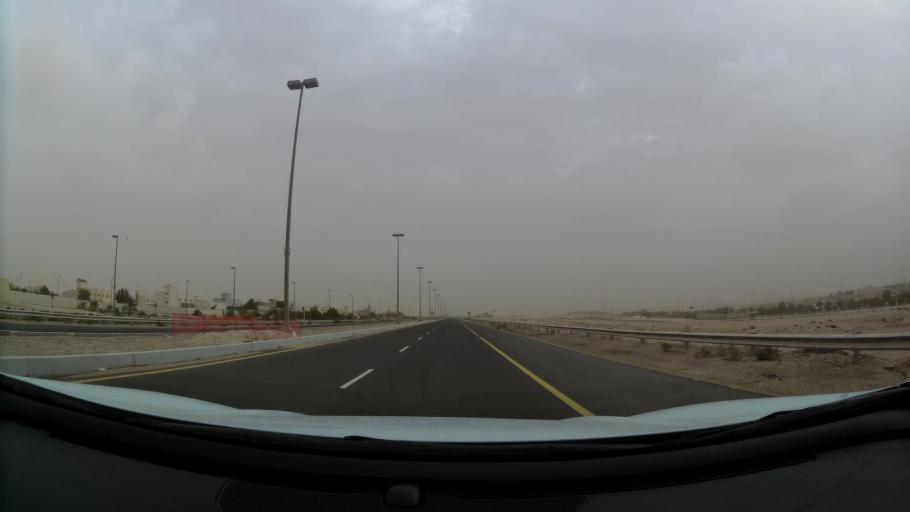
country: AE
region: Abu Dhabi
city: Abu Dhabi
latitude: 24.4211
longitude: 54.7500
